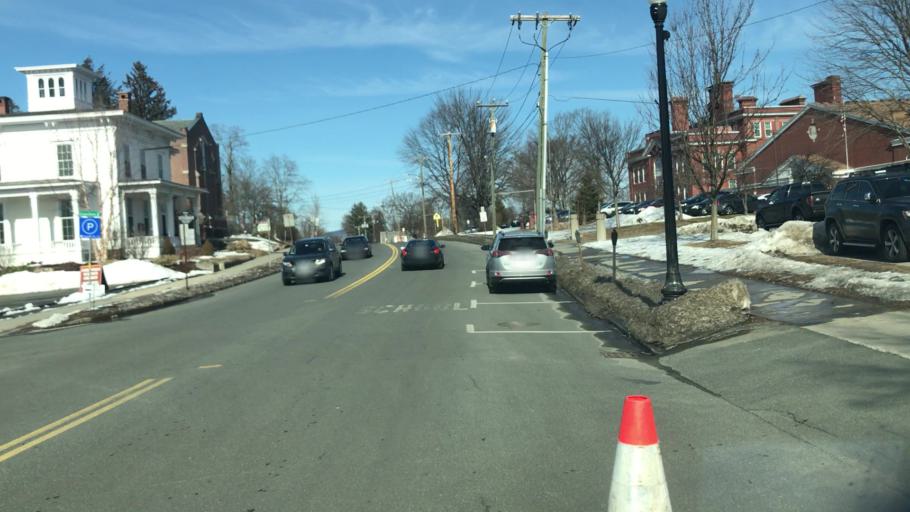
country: US
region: Massachusetts
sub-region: Franklin County
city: Greenfield
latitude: 42.5907
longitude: -72.5987
